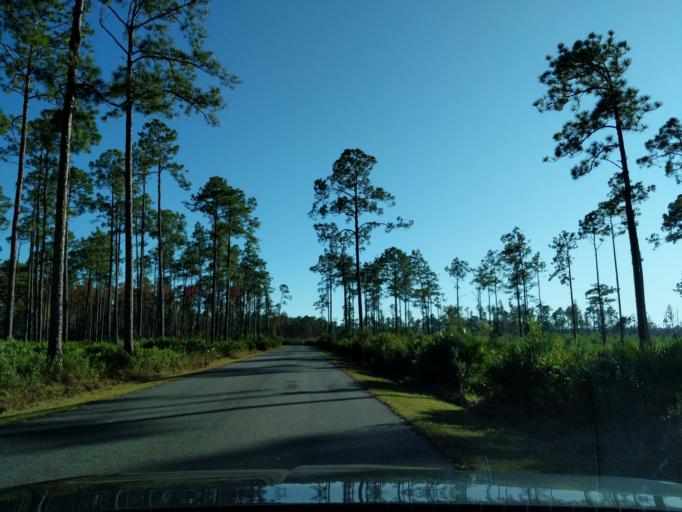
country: US
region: Georgia
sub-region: Charlton County
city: Folkston
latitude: 30.7244
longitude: -82.1399
